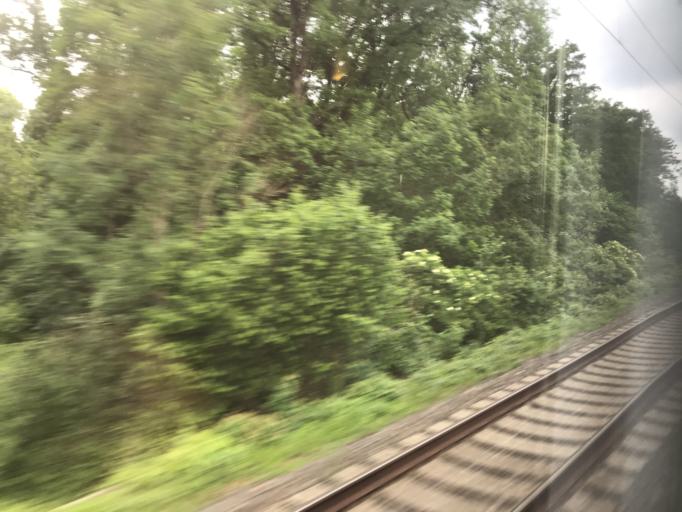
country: DE
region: Bavaria
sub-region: Swabia
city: Guenzburg
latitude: 48.4594
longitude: 10.2610
